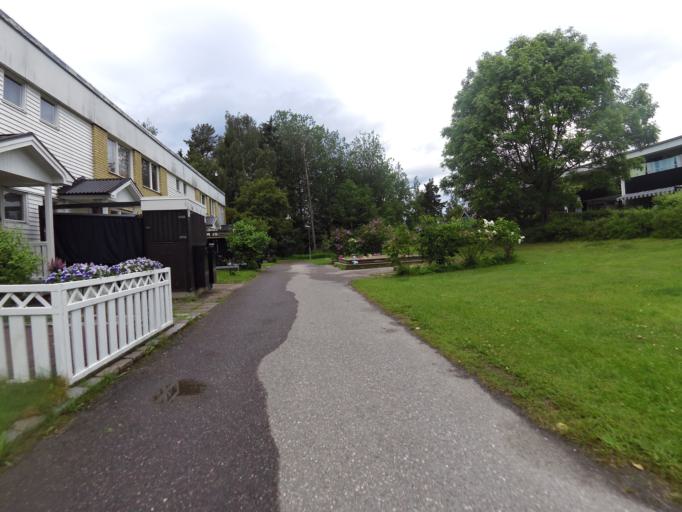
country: SE
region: Gaevleborg
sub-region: Gavle Kommun
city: Gavle
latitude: 60.6972
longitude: 17.1127
